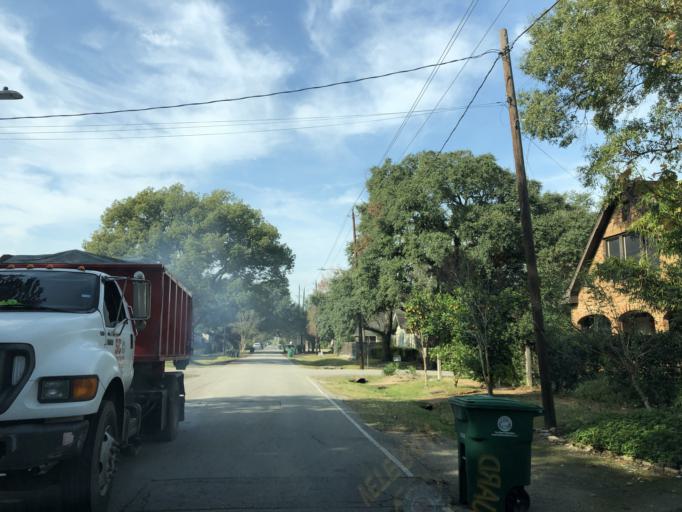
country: US
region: Texas
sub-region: Harris County
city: Houston
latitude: 29.7943
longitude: -95.4018
